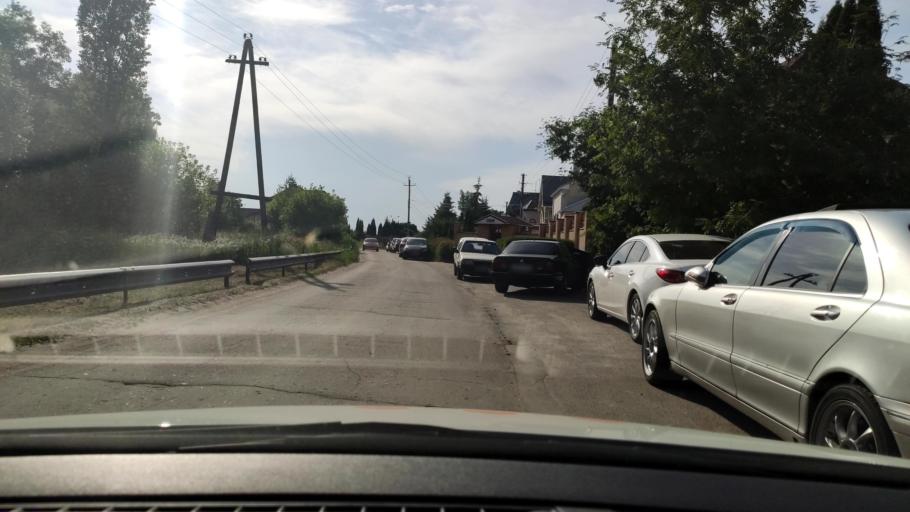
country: RU
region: Voronezj
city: Novaya Usman'
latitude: 51.6290
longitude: 39.4200
